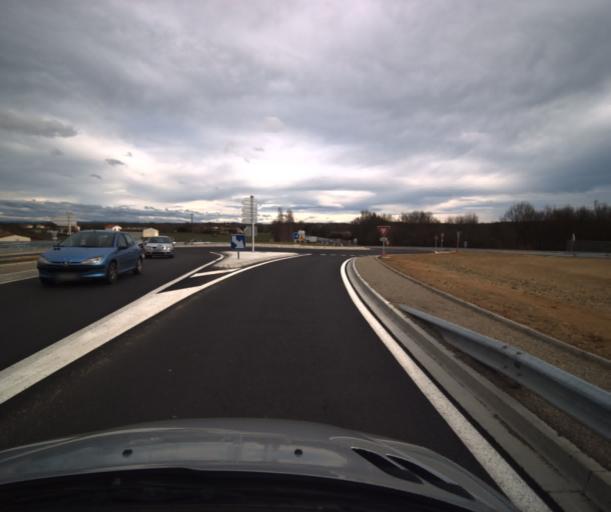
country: FR
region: Midi-Pyrenees
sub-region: Departement du Tarn-et-Garonne
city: Montauban
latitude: 44.0317
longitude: 1.3883
